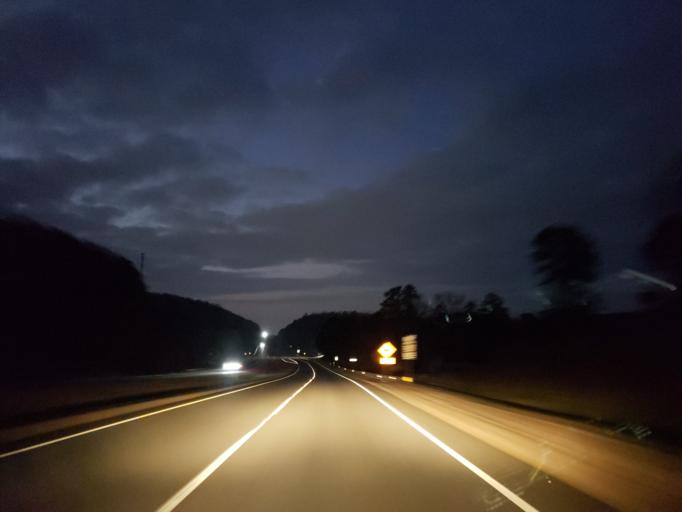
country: US
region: Georgia
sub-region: Polk County
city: Rockmart
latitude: 33.9730
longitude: -85.0026
